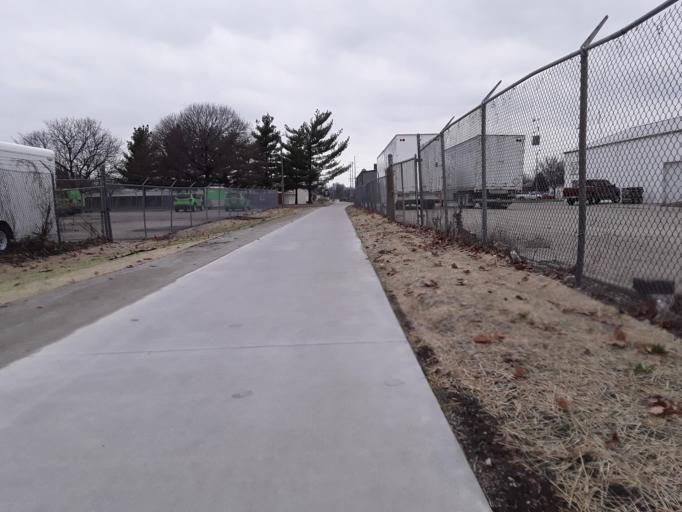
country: US
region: Nebraska
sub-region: Lancaster County
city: Lincoln
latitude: 40.8513
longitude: -96.6390
